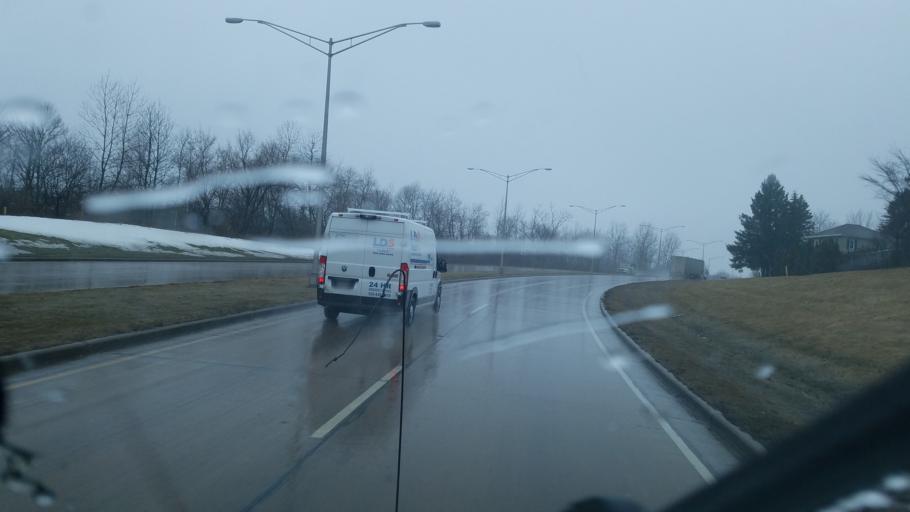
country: US
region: Wisconsin
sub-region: Wood County
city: Marshfield
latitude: 44.6722
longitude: -90.1844
